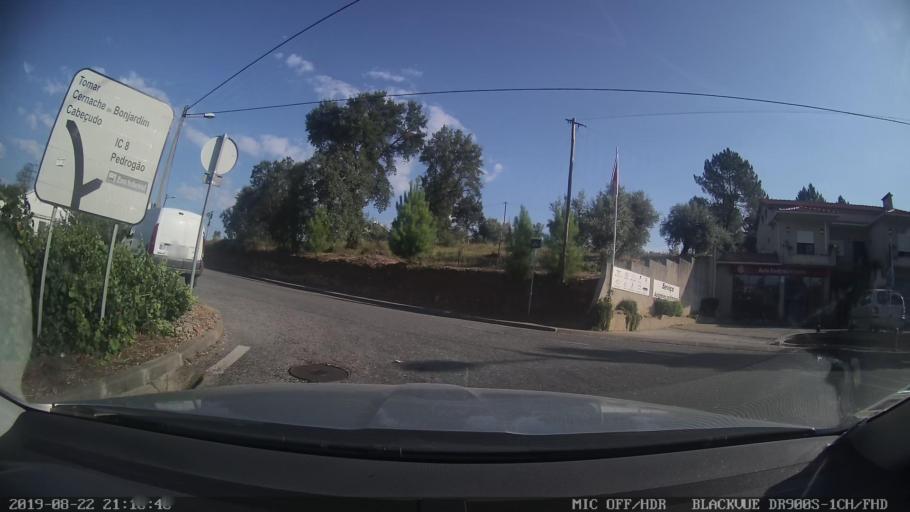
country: PT
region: Castelo Branco
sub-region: Serta
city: Serta
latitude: 39.8037
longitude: -8.1076
